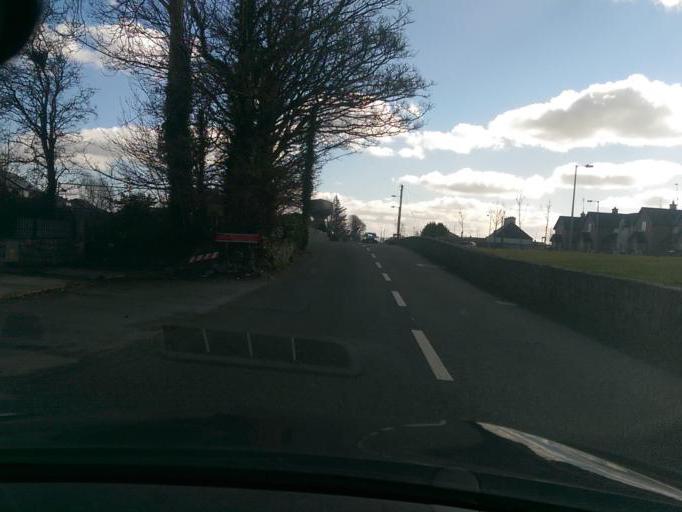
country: IE
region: Connaught
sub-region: County Galway
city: Athenry
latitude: 53.3079
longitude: -8.7529
